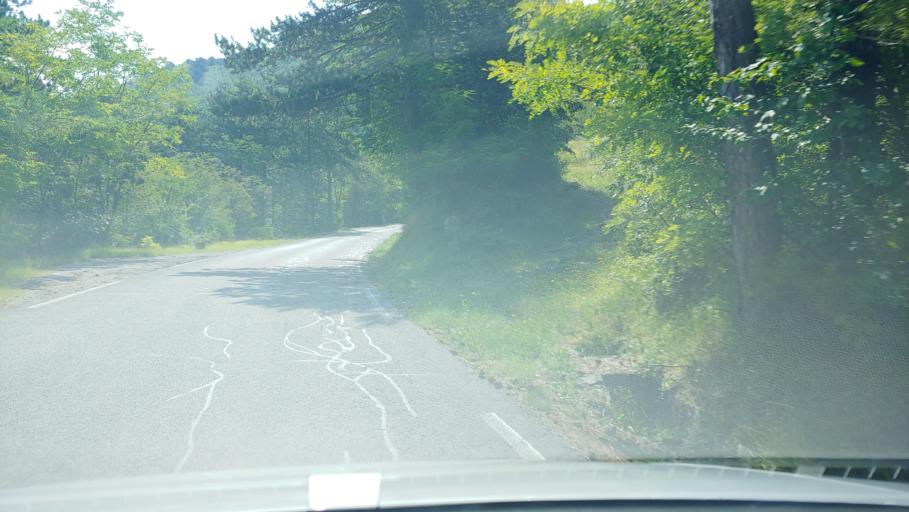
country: SI
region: Komen
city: Komen
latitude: 45.8497
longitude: 13.7874
